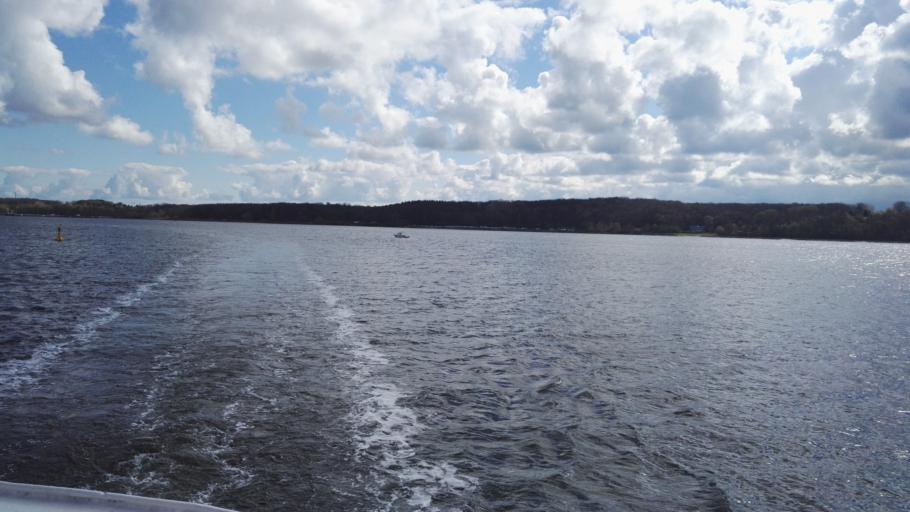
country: DE
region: Schleswig-Holstein
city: Heikendorf
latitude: 54.3847
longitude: 10.1861
